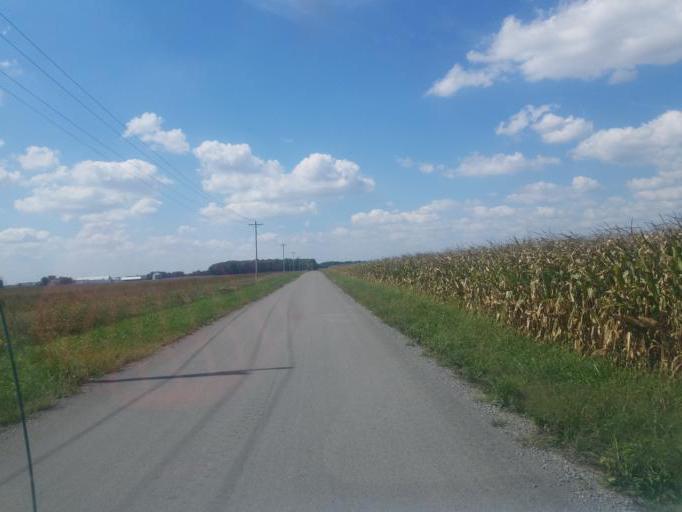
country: US
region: Ohio
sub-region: Hardin County
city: Ada
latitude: 40.6601
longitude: -83.8429
